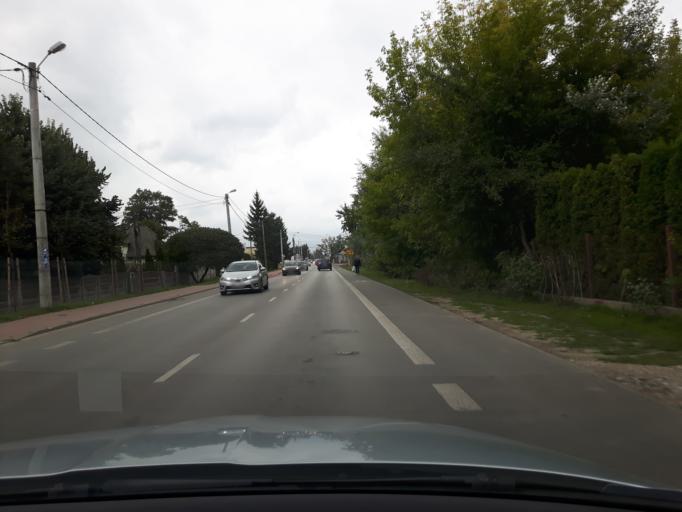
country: PL
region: Masovian Voivodeship
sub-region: Powiat wolominski
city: Kobylka
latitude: 52.3246
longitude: 21.1909
